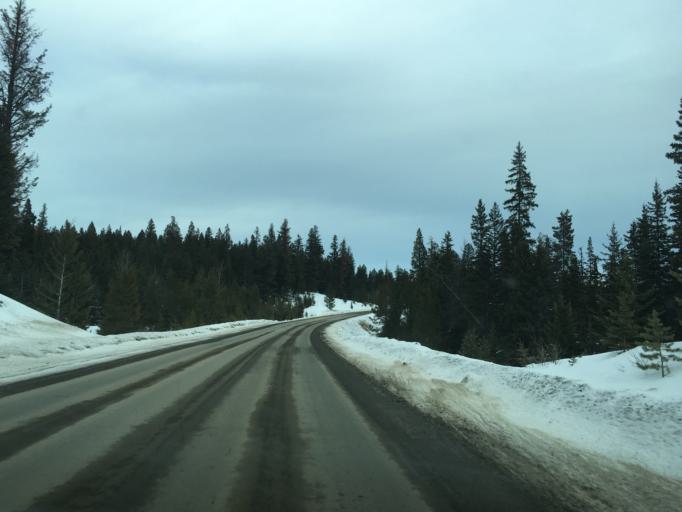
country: CA
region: British Columbia
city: Kamloops
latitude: 50.5245
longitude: -120.4674
